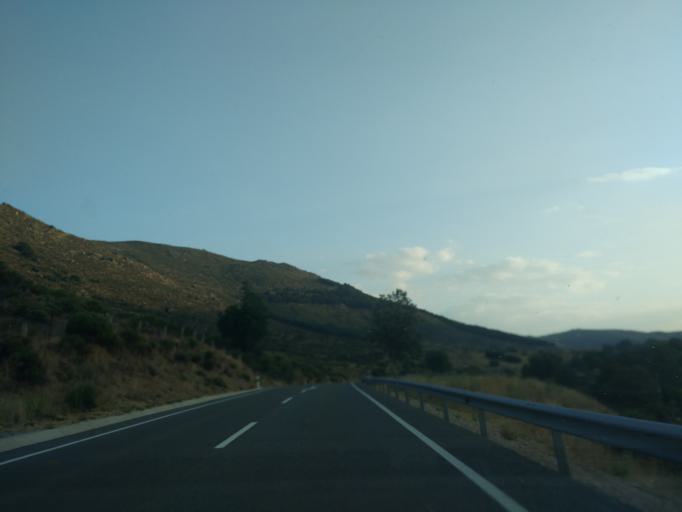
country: ES
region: Castille and Leon
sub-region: Provincia de Avila
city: Mengamunoz
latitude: 40.5059
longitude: -4.9930
